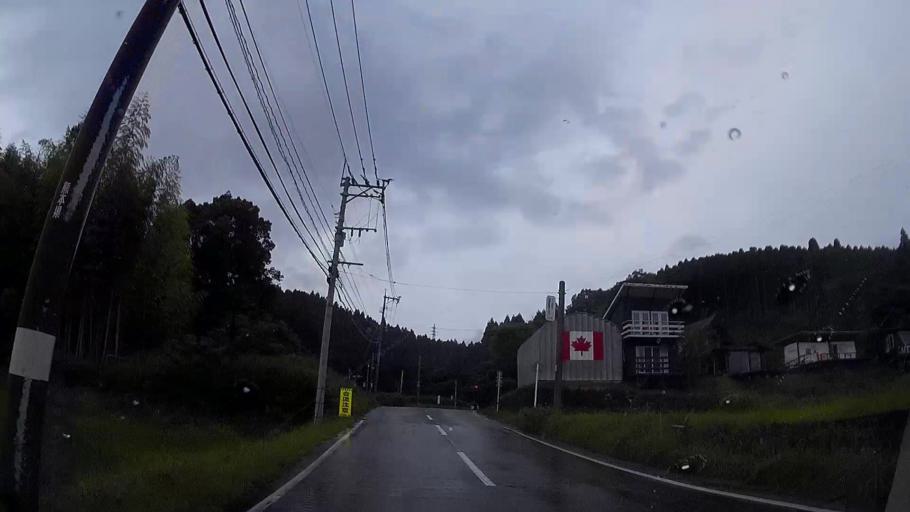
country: JP
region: Kumamoto
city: Aso
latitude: 32.8540
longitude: 131.0182
